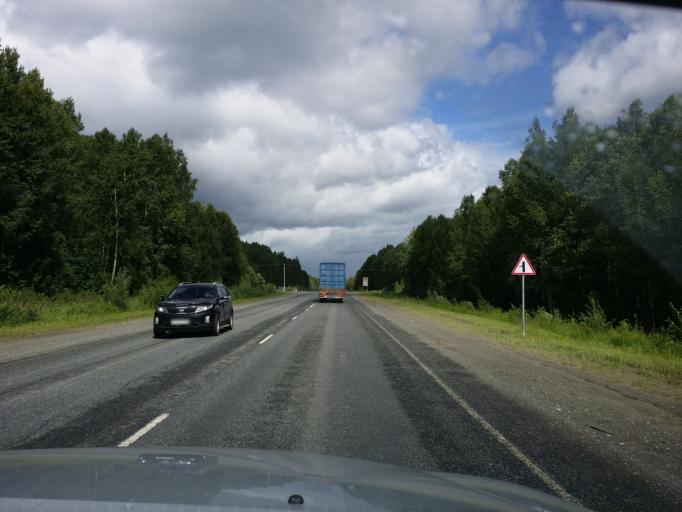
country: RU
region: Tjumen
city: Turtas
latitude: 58.9116
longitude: 69.0586
